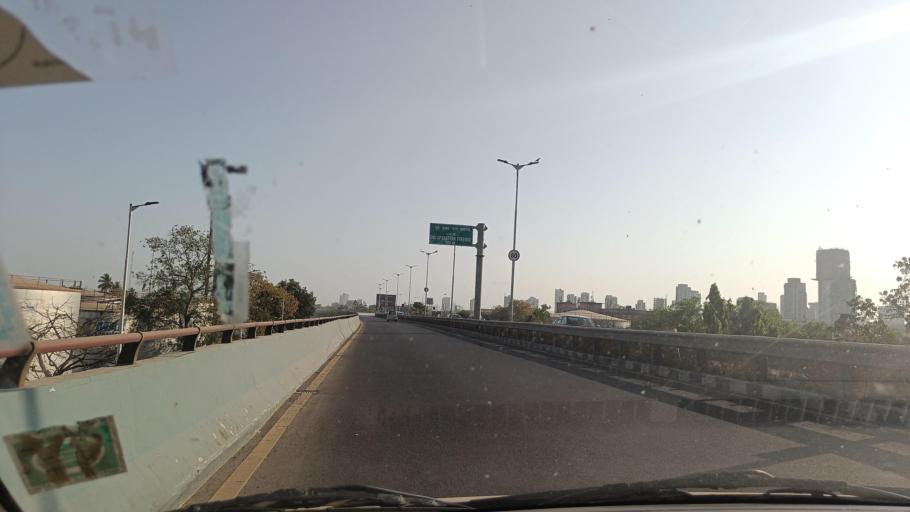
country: IN
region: Maharashtra
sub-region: Mumbai Suburban
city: Mumbai
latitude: 18.9624
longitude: 72.8449
